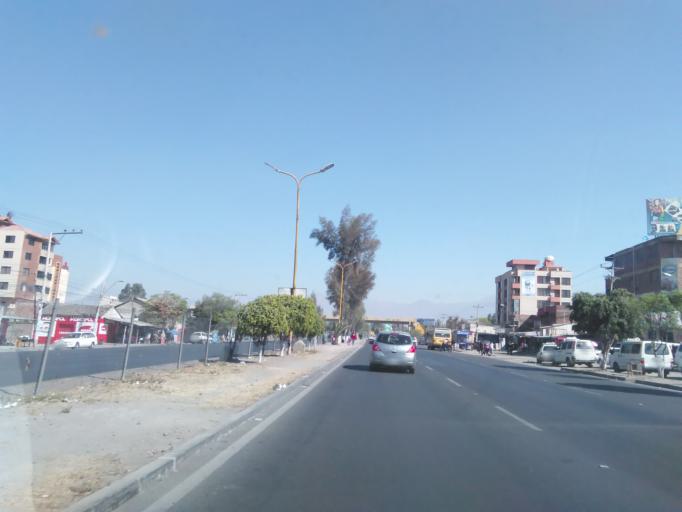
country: BO
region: Cochabamba
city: Cochabamba
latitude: -17.3908
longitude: -66.2415
